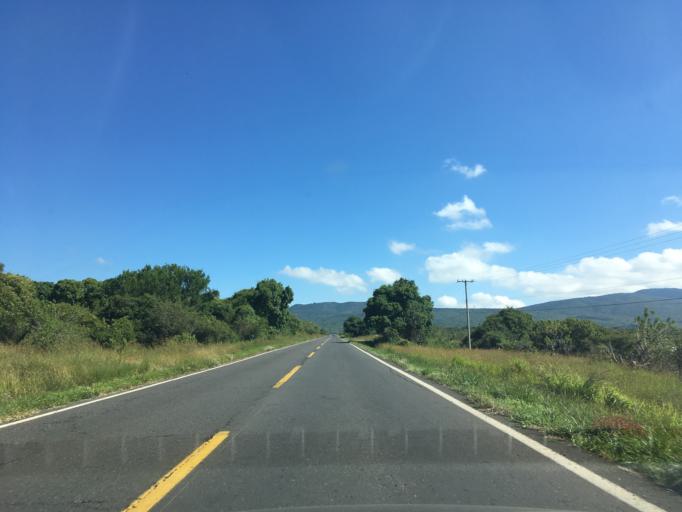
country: MX
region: Mexico
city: Tlazazalca
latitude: 19.9962
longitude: -102.0556
